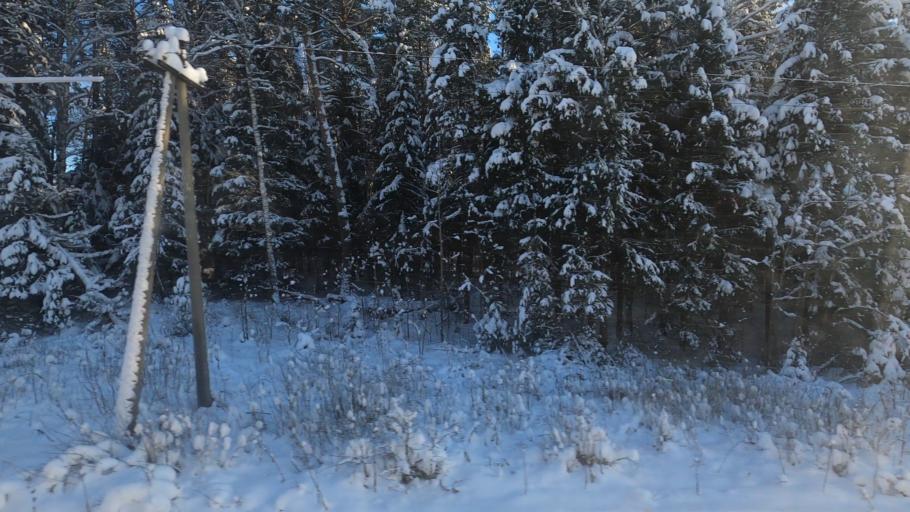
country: RU
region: Moskovskaya
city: Novo-Nikol'skoye
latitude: 56.5517
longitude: 37.5637
